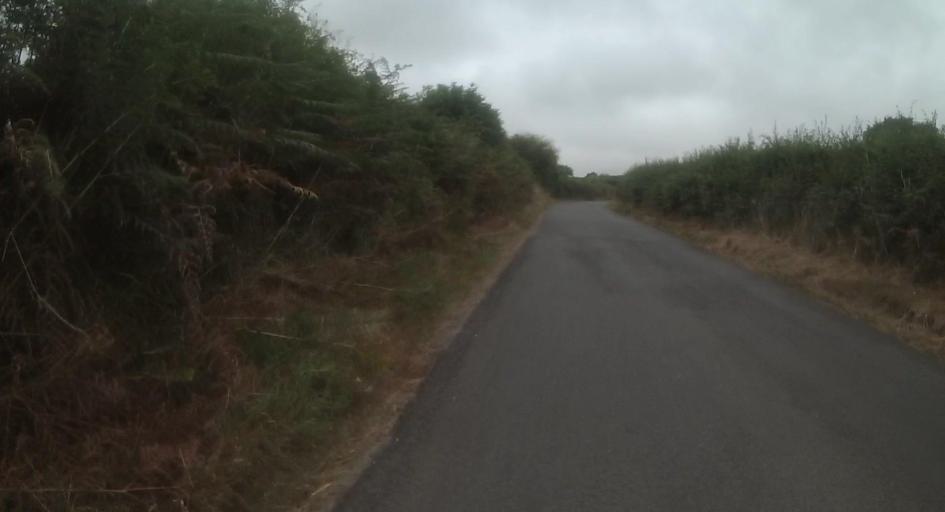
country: GB
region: England
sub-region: Dorset
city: Bovington Camp
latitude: 50.7373
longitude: -2.2165
